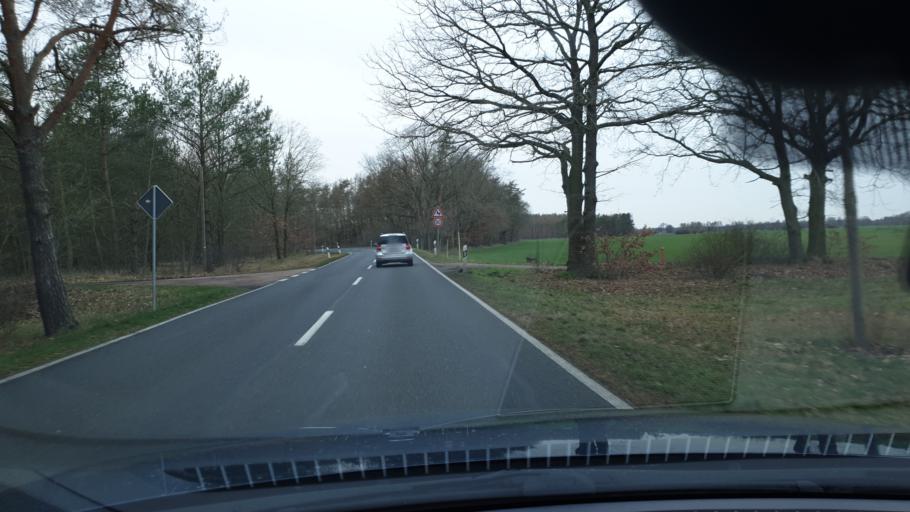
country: DE
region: Saxony-Anhalt
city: Oranienbaum
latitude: 51.7892
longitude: 12.4424
